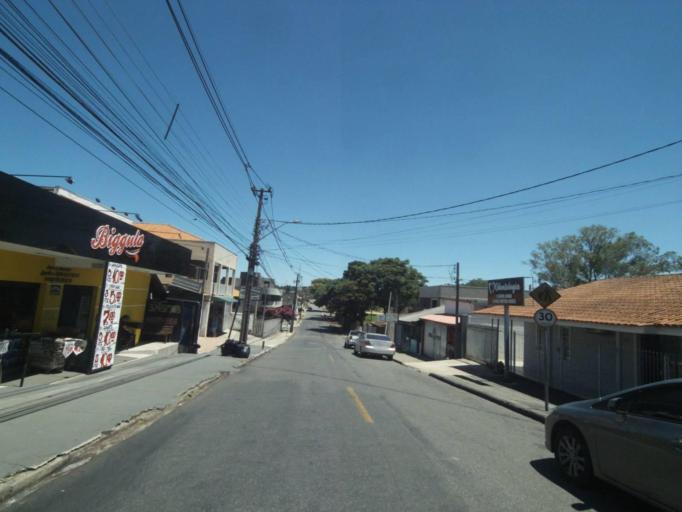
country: BR
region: Parana
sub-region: Curitiba
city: Curitiba
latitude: -25.4757
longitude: -49.3393
